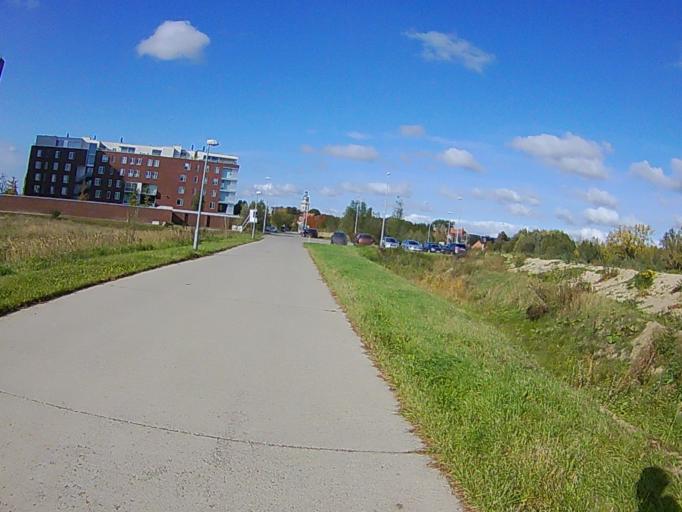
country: BE
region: Flanders
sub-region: Provincie Antwerpen
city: Niel
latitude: 51.1267
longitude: 4.2983
